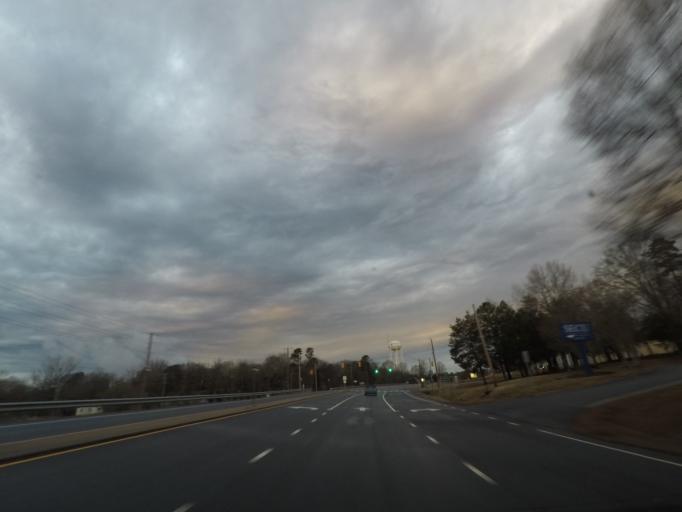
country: US
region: North Carolina
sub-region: Caswell County
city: Yanceyville
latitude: 36.4077
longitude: -79.3356
